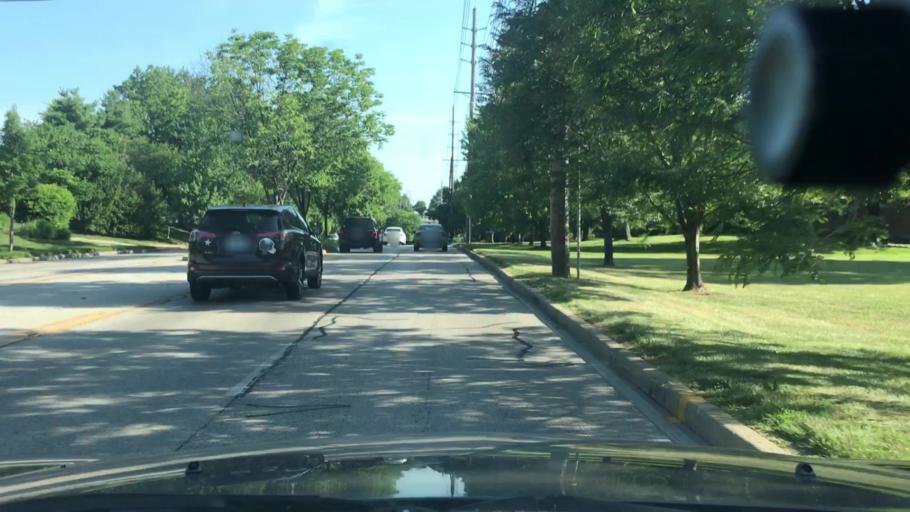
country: US
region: Missouri
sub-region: Saint Louis County
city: Creve Coeur
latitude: 38.6515
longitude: -90.4433
